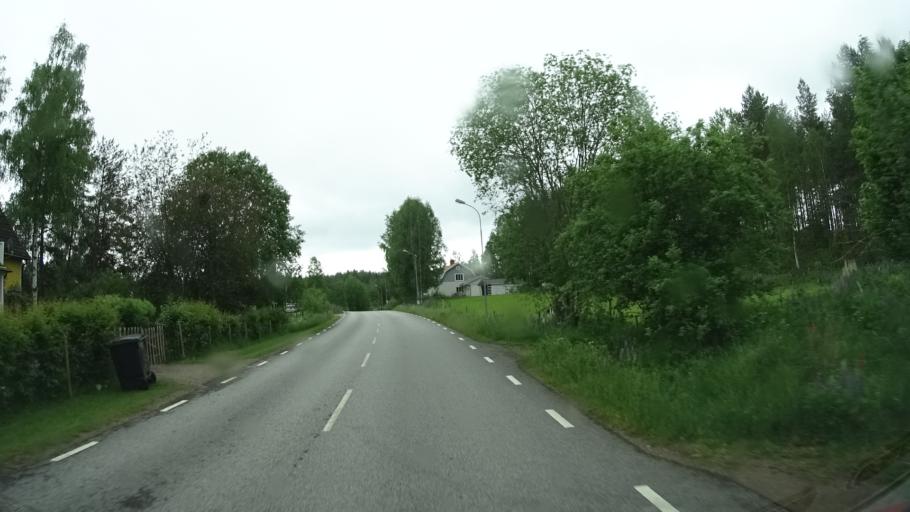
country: SE
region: Joenkoeping
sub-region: Eksjo Kommun
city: Mariannelund
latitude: 57.6852
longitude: 15.6221
